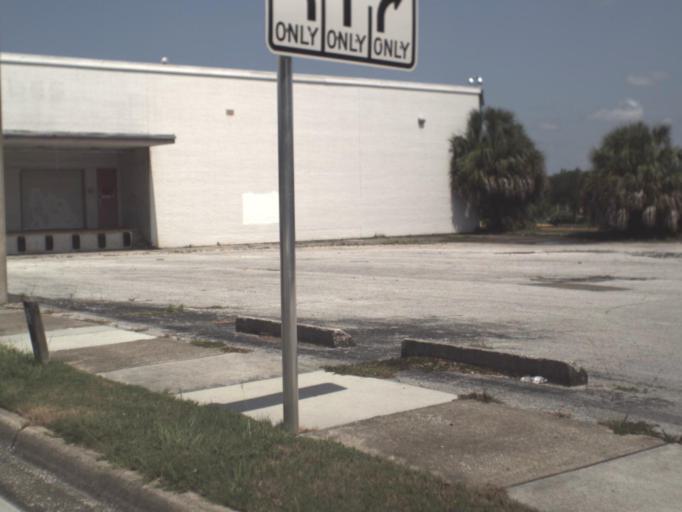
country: US
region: Florida
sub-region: Alachua County
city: Gainesville
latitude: 29.6740
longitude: -82.3377
